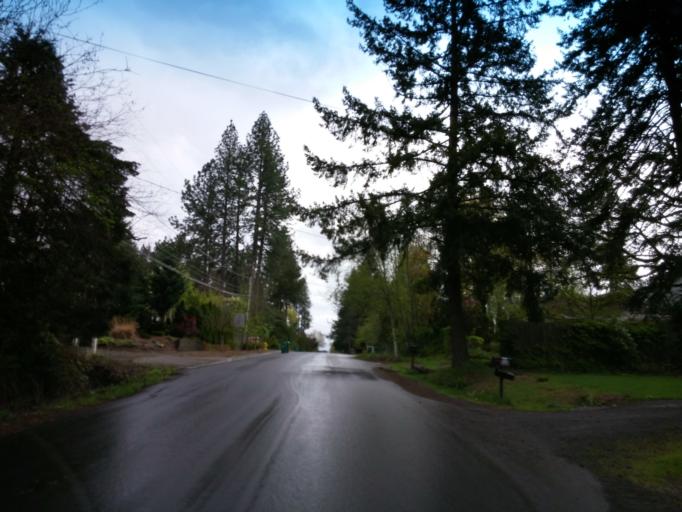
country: US
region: Oregon
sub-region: Washington County
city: Cedar Mill
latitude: 45.5207
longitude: -122.8254
